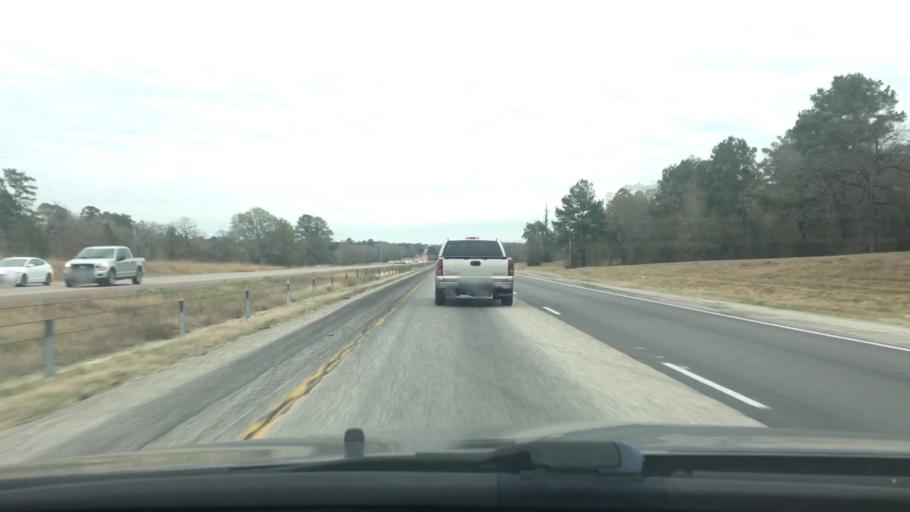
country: US
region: Texas
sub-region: Walker County
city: Huntsville
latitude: 30.7728
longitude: -95.6447
